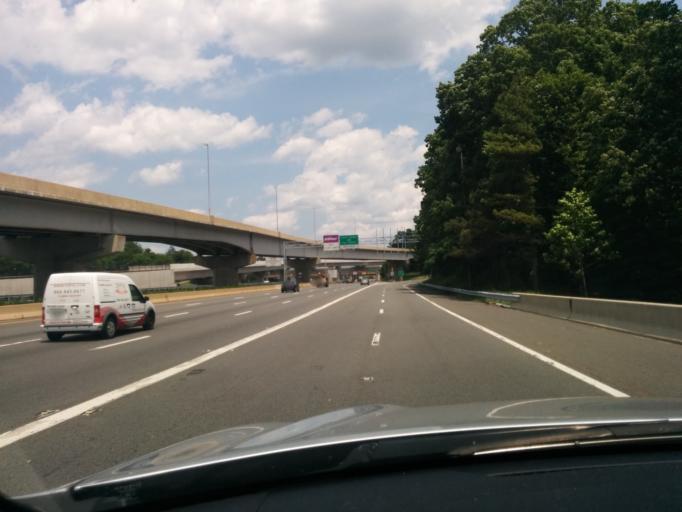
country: US
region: Virginia
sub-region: Fairfax County
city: Tysons Corner
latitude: 38.9323
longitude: -77.2519
